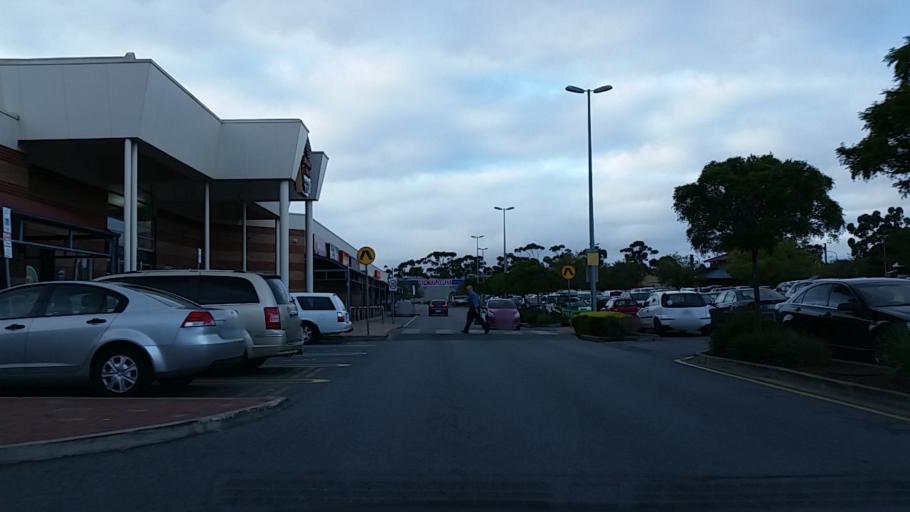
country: AU
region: South Australia
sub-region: Playford
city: Smithfield
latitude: -34.6877
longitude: 138.6893
